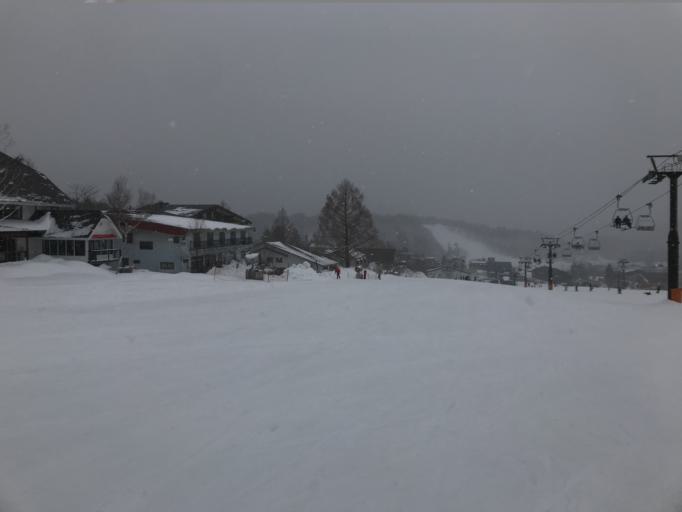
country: JP
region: Nagano
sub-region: Kitaazumi Gun
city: Hakuba
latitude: 36.7524
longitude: 137.8680
